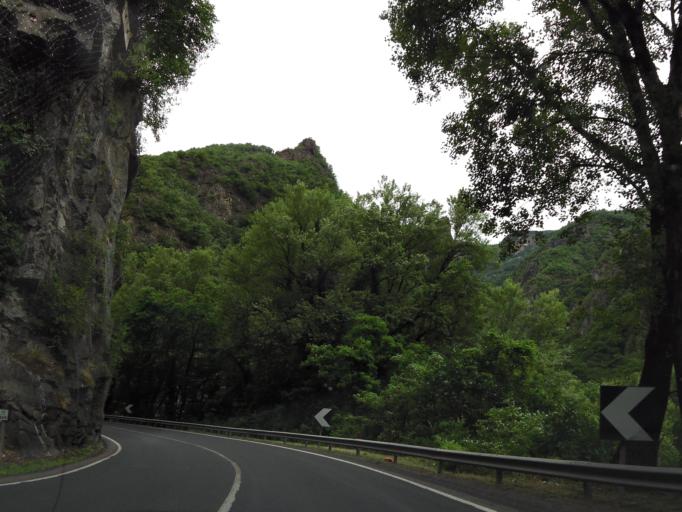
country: IT
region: Trentino-Alto Adige
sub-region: Bolzano
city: Cornedo All'Isarco
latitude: 46.4938
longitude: 11.4336
